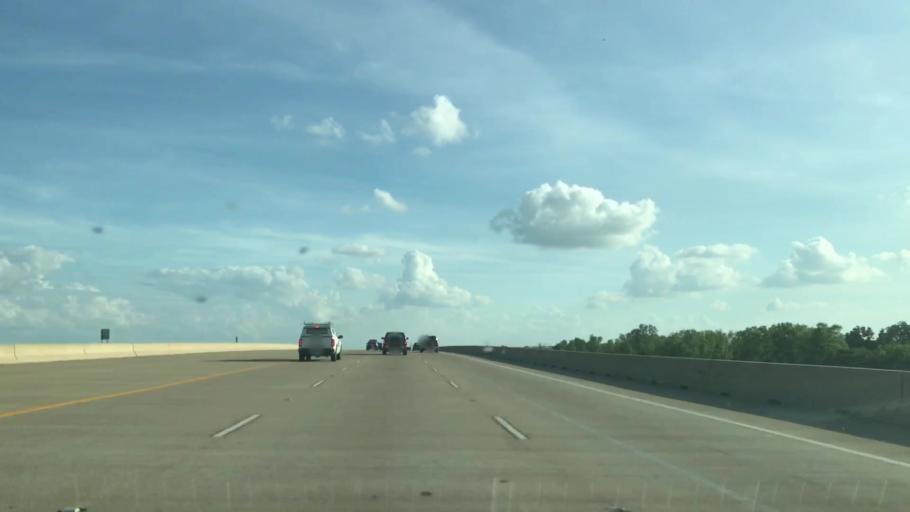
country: US
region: Texas
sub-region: Dallas County
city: Grand Prairie
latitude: 32.8031
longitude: -97.0186
